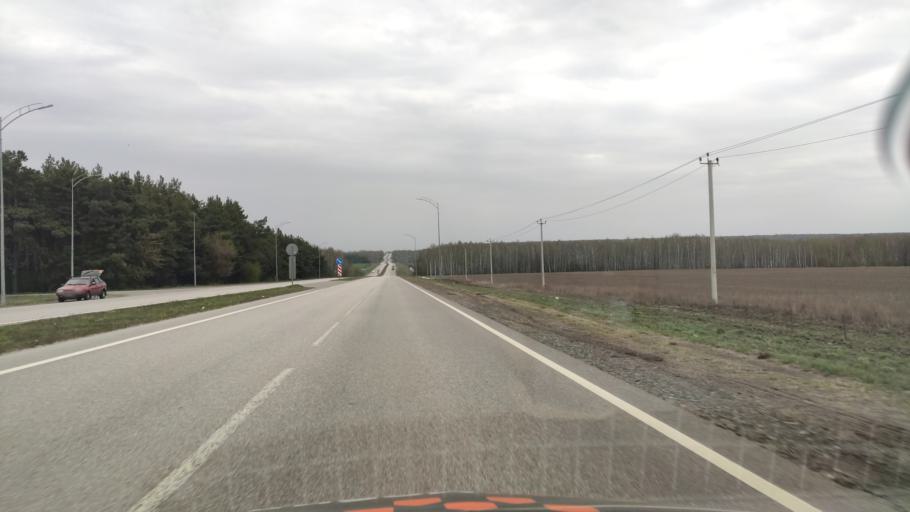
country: RU
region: Belgorod
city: Staryy Oskol
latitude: 51.3983
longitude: 37.8740
